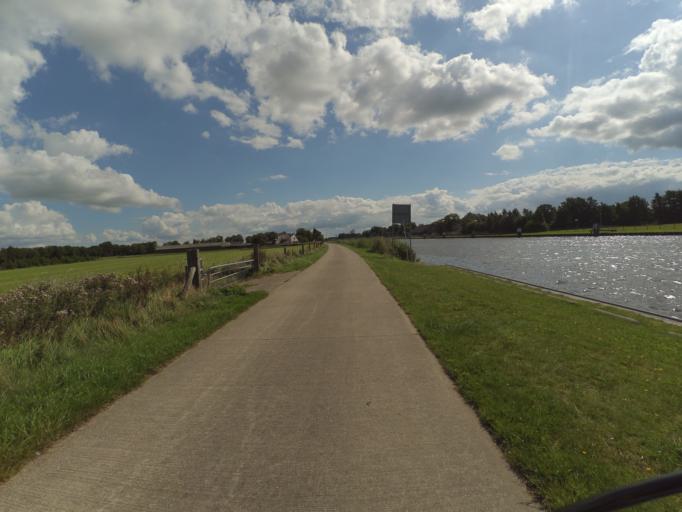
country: NL
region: Friesland
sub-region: Gemeente Tytsjerksteradiel
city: Eastermar
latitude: 53.2005
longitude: 6.0642
